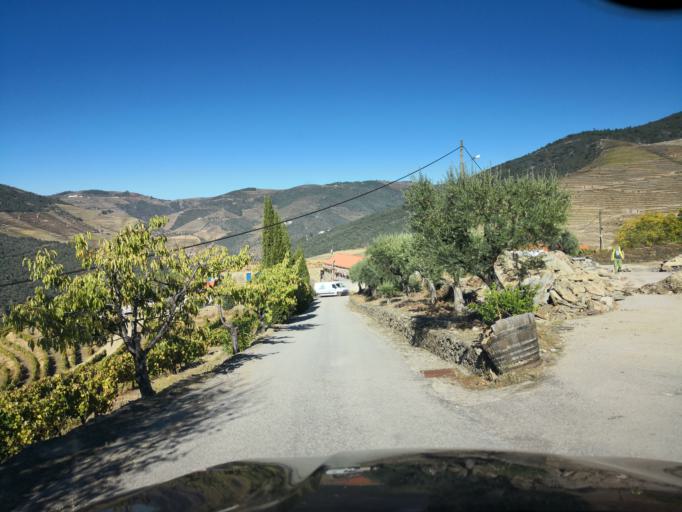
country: PT
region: Viseu
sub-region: Tabuaco
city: Tabuaco
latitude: 41.1757
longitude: -7.5155
